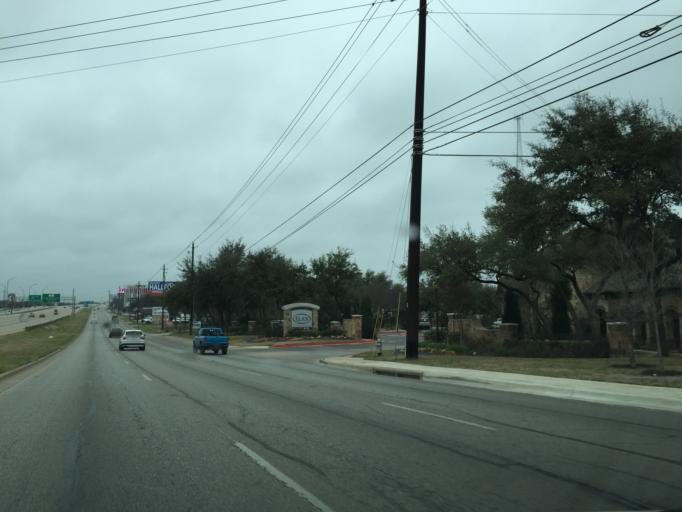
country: US
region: Texas
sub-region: Williamson County
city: Jollyville
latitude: 30.4407
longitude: -97.7805
